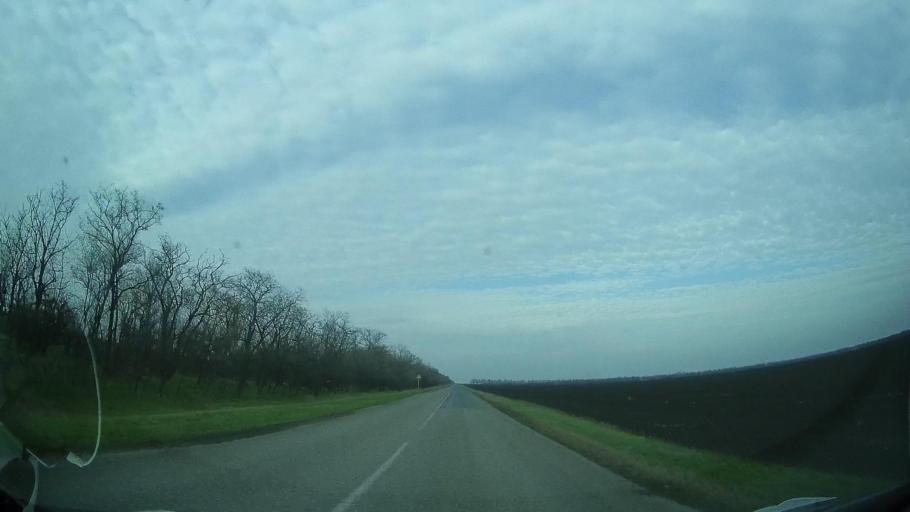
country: RU
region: Rostov
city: Zernograd
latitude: 46.9301
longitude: 40.3665
